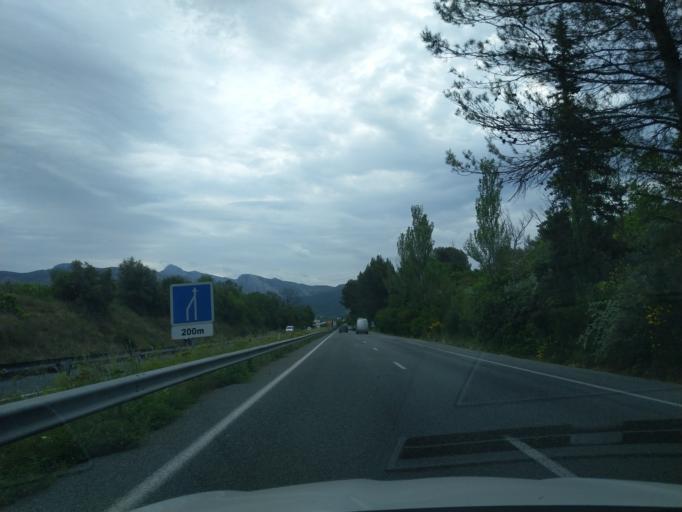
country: FR
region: Provence-Alpes-Cote d'Azur
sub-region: Departement des Bouches-du-Rhone
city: Aubagne
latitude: 43.2838
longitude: 5.5869
